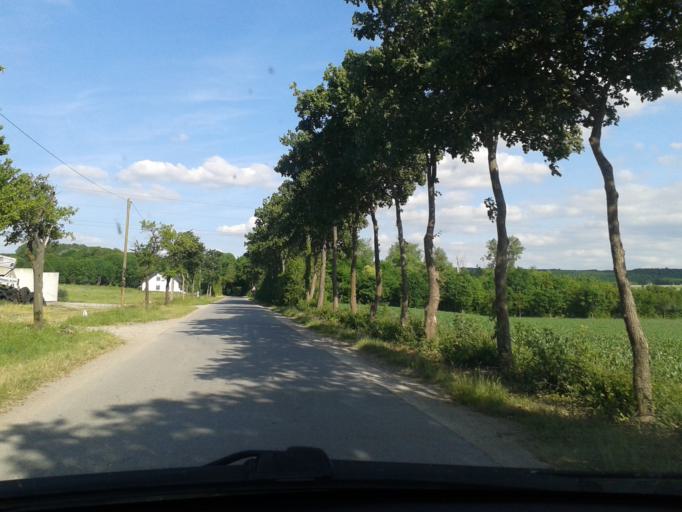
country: DE
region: North Rhine-Westphalia
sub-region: Regierungsbezirk Detmold
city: Schlangen
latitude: 51.7831
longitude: 8.8481
